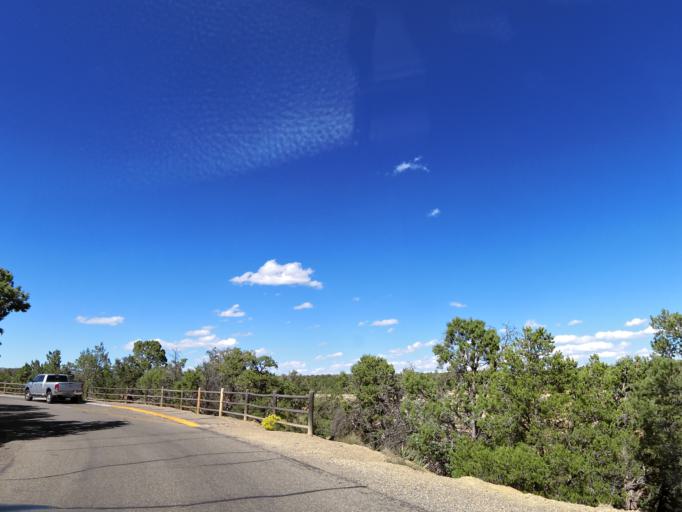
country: US
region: Colorado
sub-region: Montezuma County
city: Cortez
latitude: 37.1618
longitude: -108.4749
